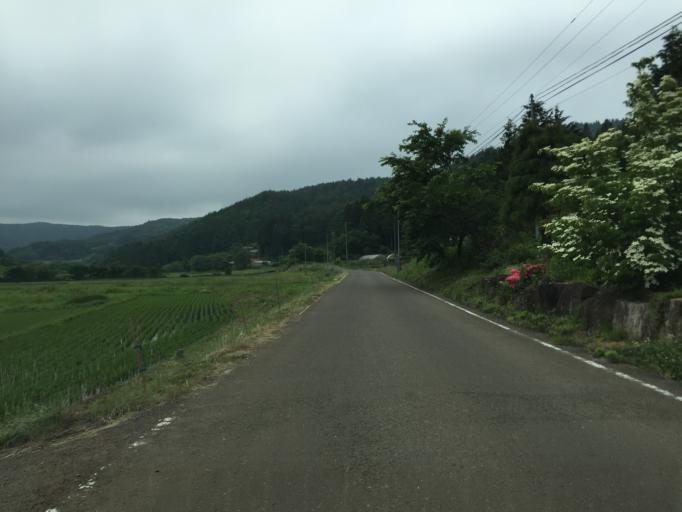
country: JP
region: Miyagi
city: Marumori
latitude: 37.7955
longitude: 140.7320
